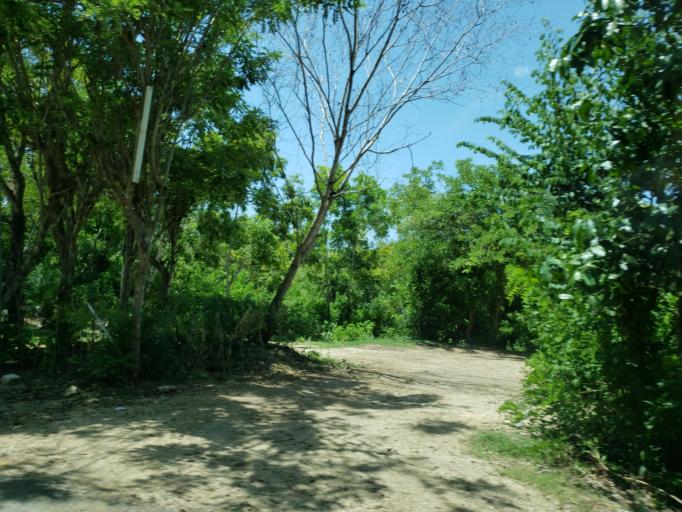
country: ID
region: Bali
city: Kangin
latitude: -8.8443
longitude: 115.1397
